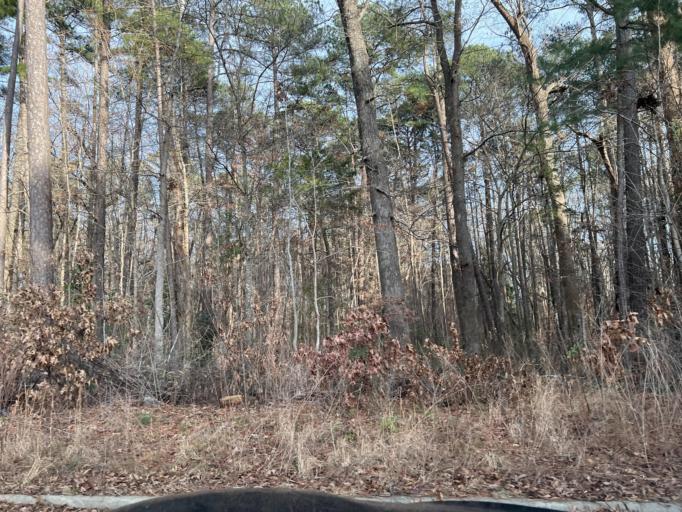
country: US
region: North Carolina
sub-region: Wake County
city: Cary
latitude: 35.7819
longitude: -78.7313
